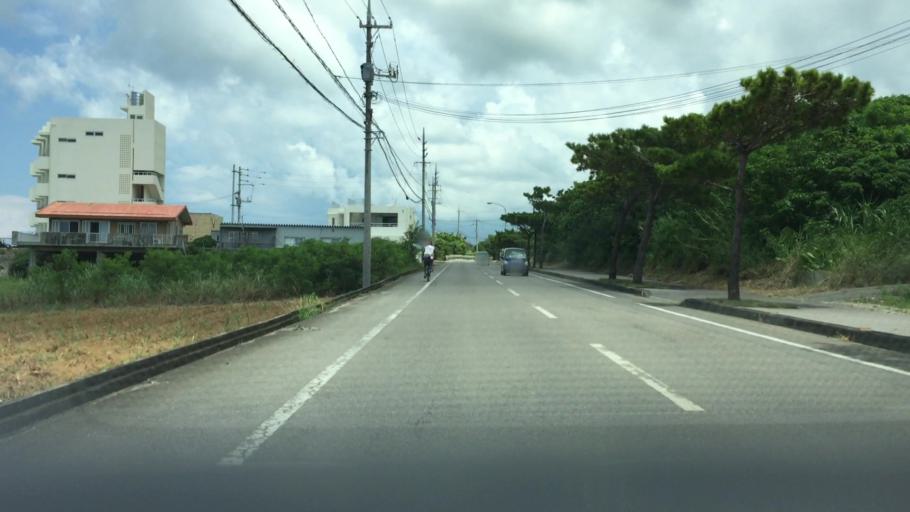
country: JP
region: Okinawa
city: Ishigaki
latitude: 24.3591
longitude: 124.1450
